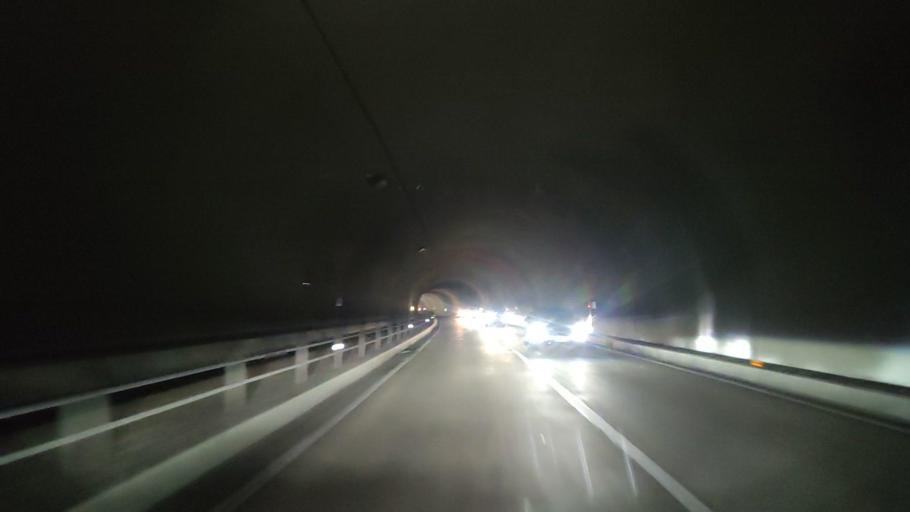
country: JP
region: Gifu
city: Godo
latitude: 35.5890
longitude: 136.6308
